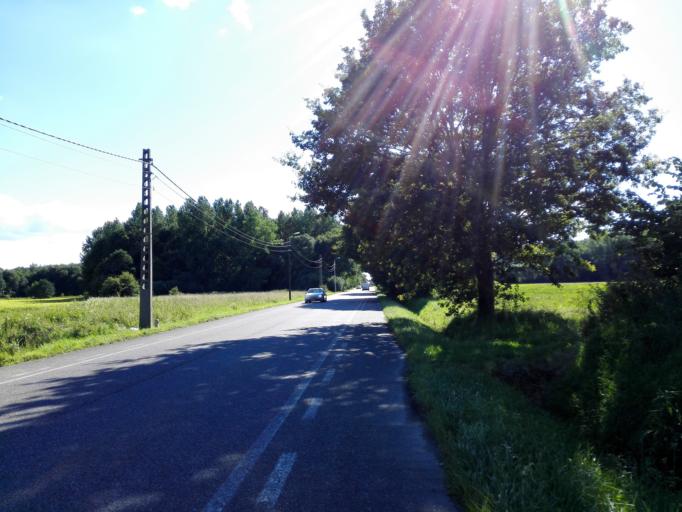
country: BE
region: Flanders
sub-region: Provincie Vlaams-Brabant
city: Tremelo
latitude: 50.9827
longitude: 4.7505
